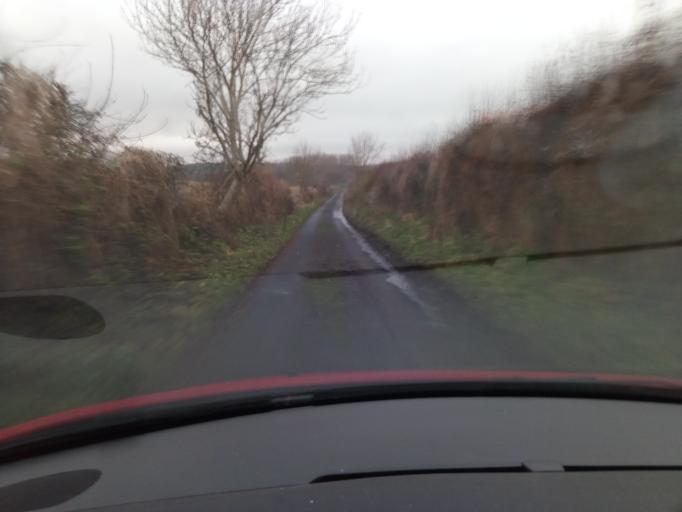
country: GB
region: Scotland
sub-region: The Scottish Borders
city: Kelso
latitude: 55.5294
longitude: -2.4649
